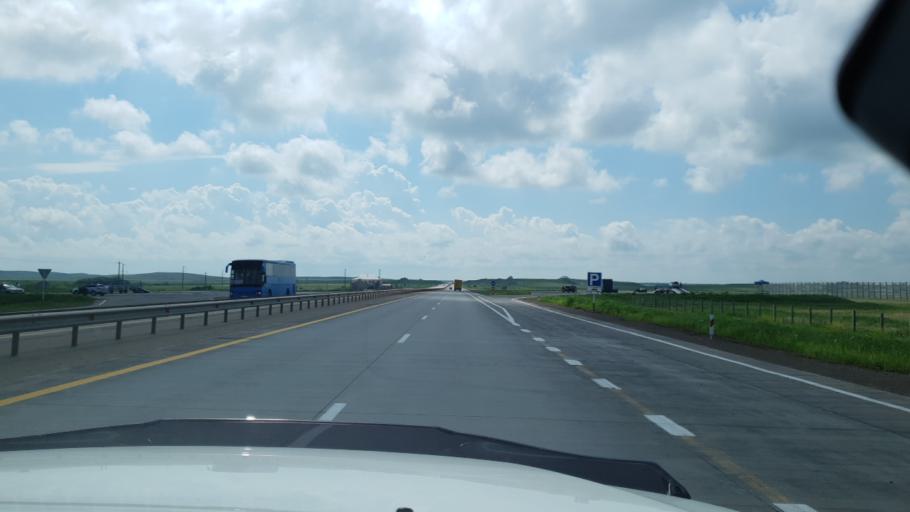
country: KZ
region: Qaraghandy
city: Osakarovka
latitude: 50.7957
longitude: 72.2138
